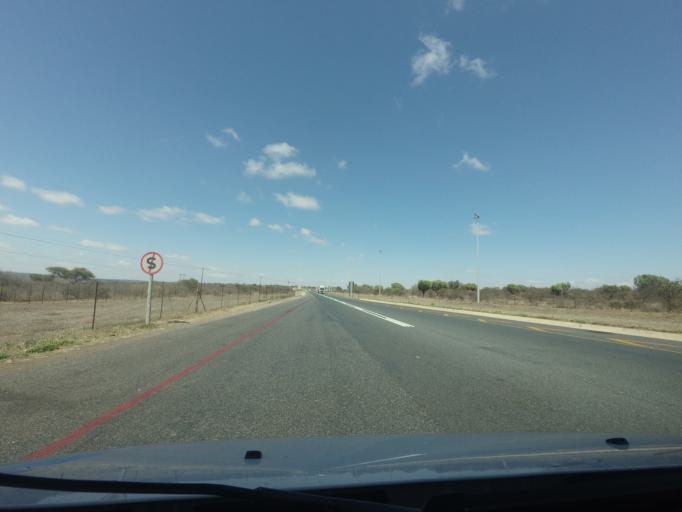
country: ZA
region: Limpopo
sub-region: Vhembe District Municipality
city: Louis Trichardt
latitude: -23.3681
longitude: 29.7741
